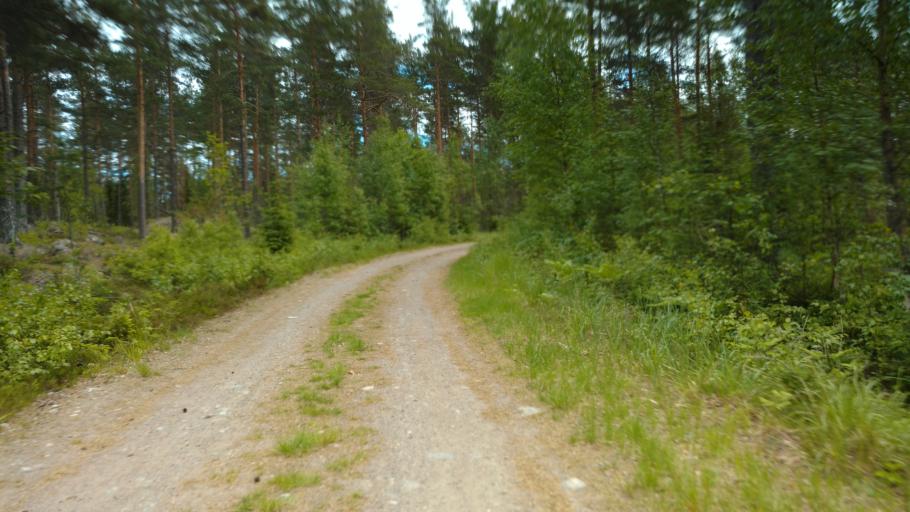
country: FI
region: Uusimaa
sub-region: Raaseporin
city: Pohja
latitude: 60.1150
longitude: 23.5519
